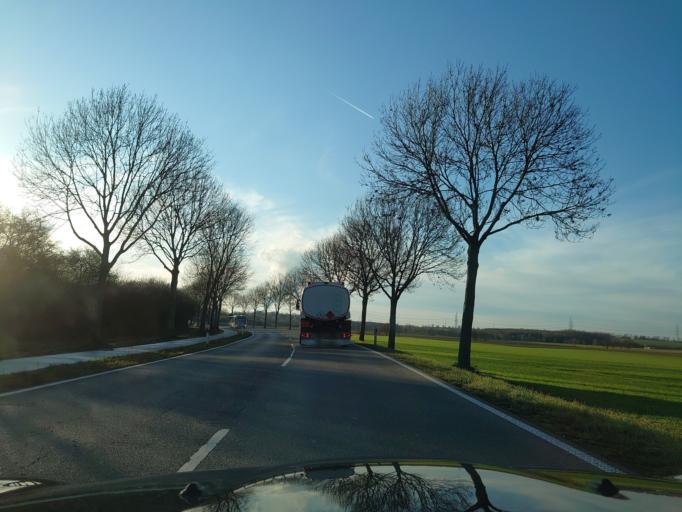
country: DE
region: North Rhine-Westphalia
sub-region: Regierungsbezirk Dusseldorf
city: Rommerskirchen
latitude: 51.0705
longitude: 6.7464
